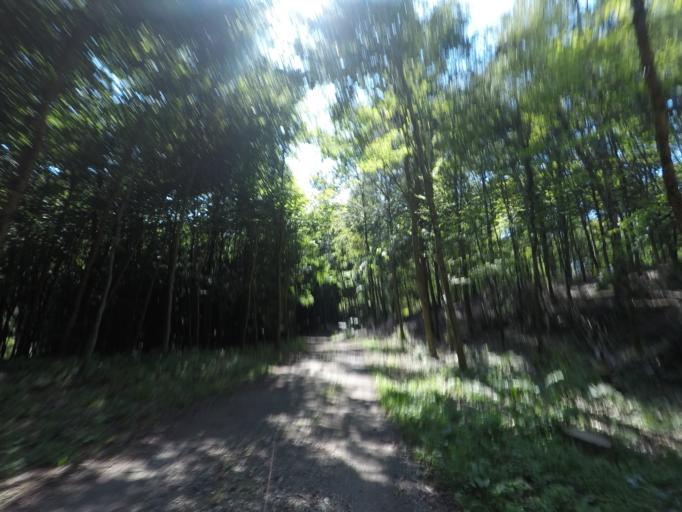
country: LU
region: Luxembourg
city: Bridel
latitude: 49.6435
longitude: 6.0772
